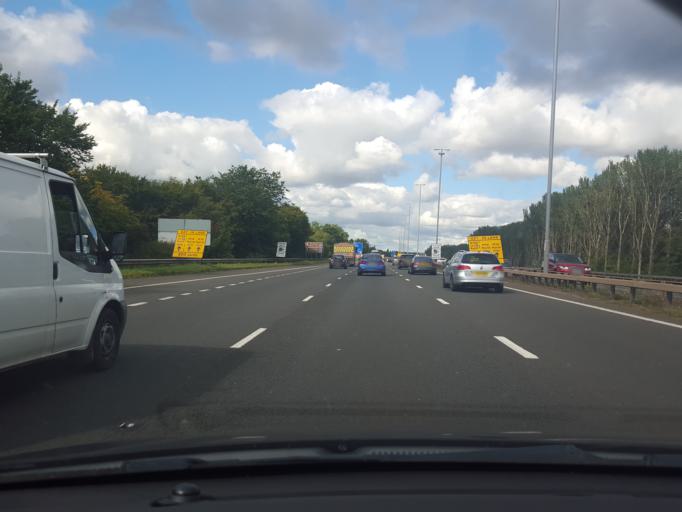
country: GB
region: Scotland
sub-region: South Lanarkshire
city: Hamilton
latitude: 55.7921
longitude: -4.0403
